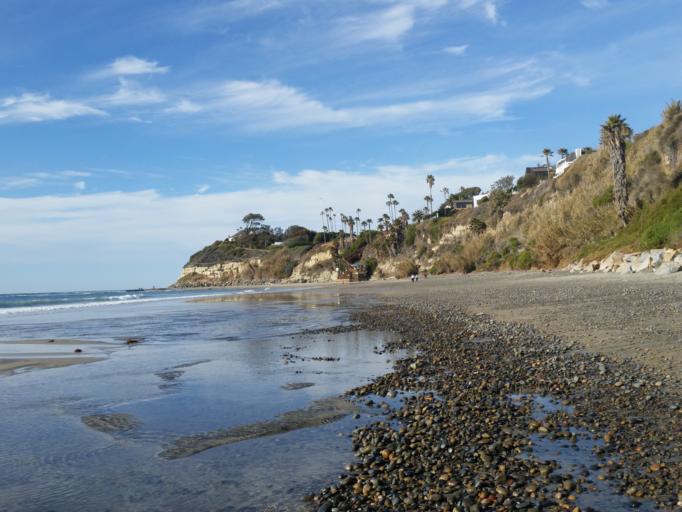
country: US
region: California
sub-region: San Diego County
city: Encinitas
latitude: 33.0319
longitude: -117.2905
